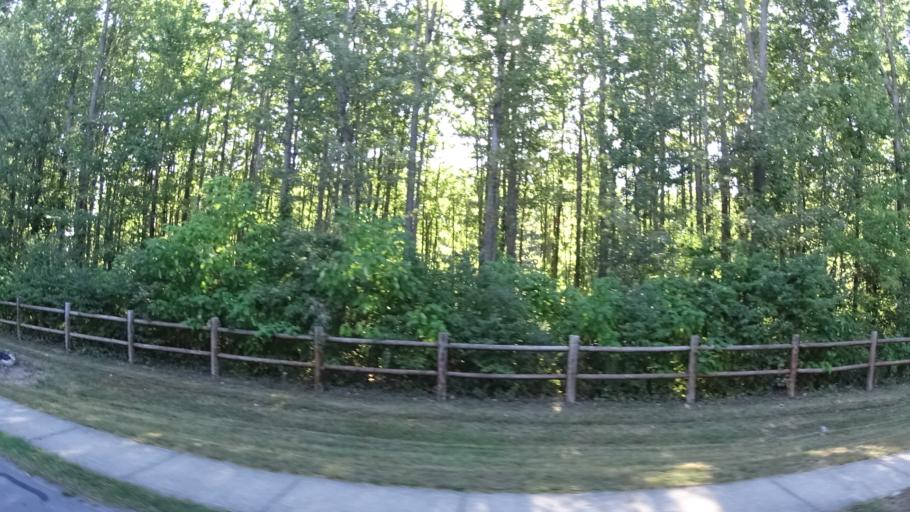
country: US
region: Ohio
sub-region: Erie County
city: Sandusky
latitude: 41.6133
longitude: -82.7069
